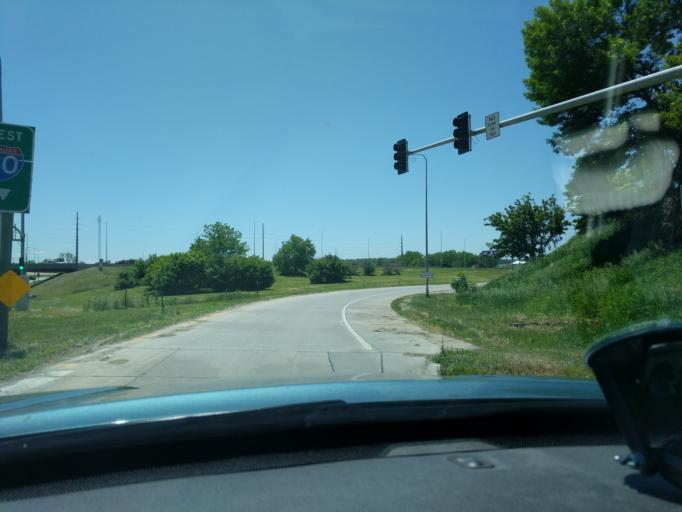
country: US
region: Nebraska
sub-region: Douglas County
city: Ralston
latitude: 41.2254
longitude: -96.0241
